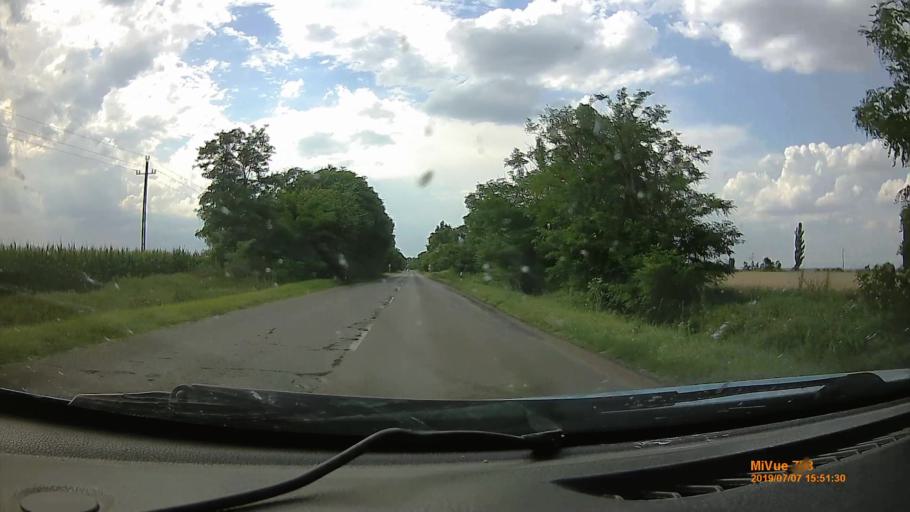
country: HU
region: Jasz-Nagykun-Szolnok
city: Jaszbereny
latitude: 47.5335
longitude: 19.8379
